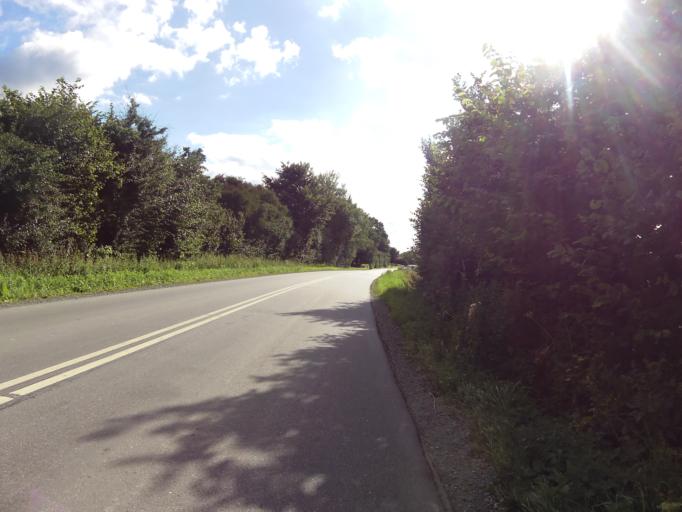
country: DK
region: South Denmark
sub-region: Haderslev Kommune
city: Haderslev
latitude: 55.2035
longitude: 9.4035
